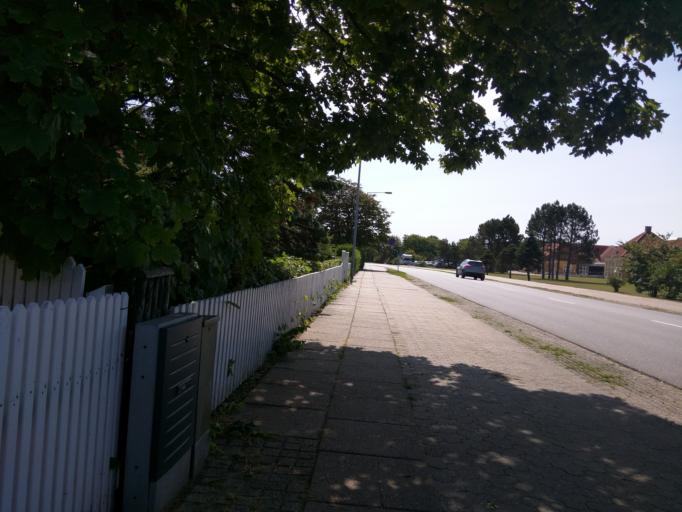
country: DK
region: North Denmark
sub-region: Frederikshavn Kommune
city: Skagen
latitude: 57.7205
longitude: 10.5764
